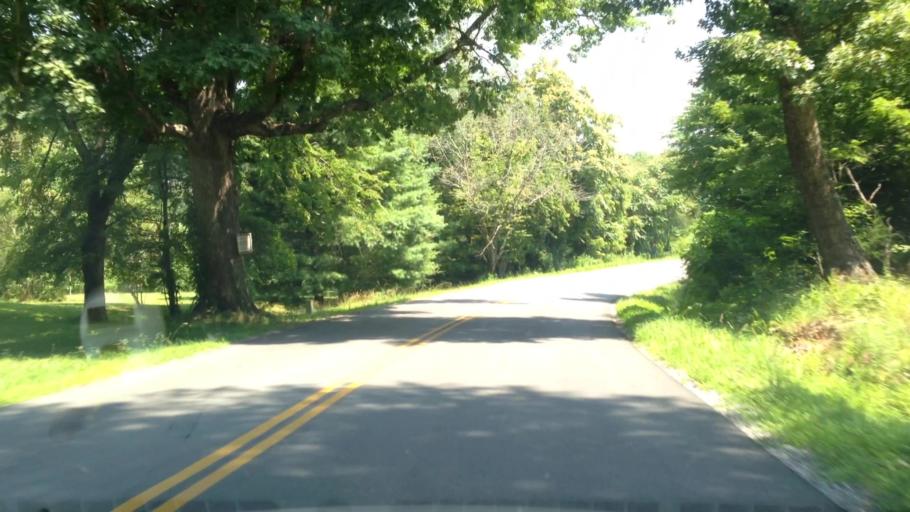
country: US
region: Virginia
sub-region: Patrick County
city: Patrick Springs
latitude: 36.5829
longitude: -80.1910
